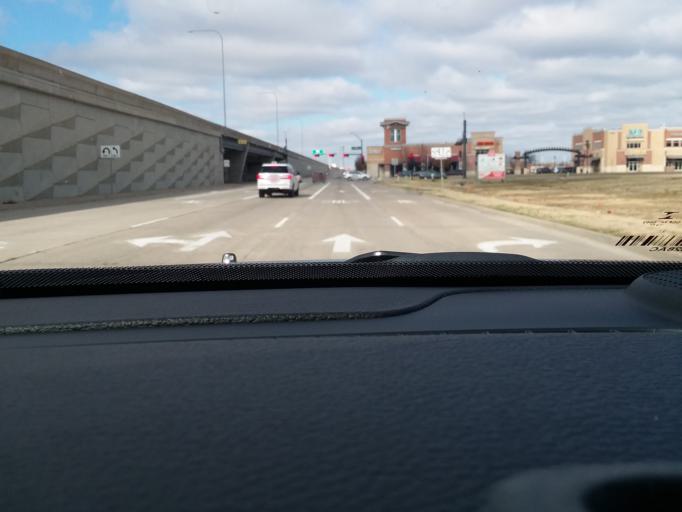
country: US
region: Texas
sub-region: Collin County
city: Frisco
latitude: 33.1516
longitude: -96.8396
